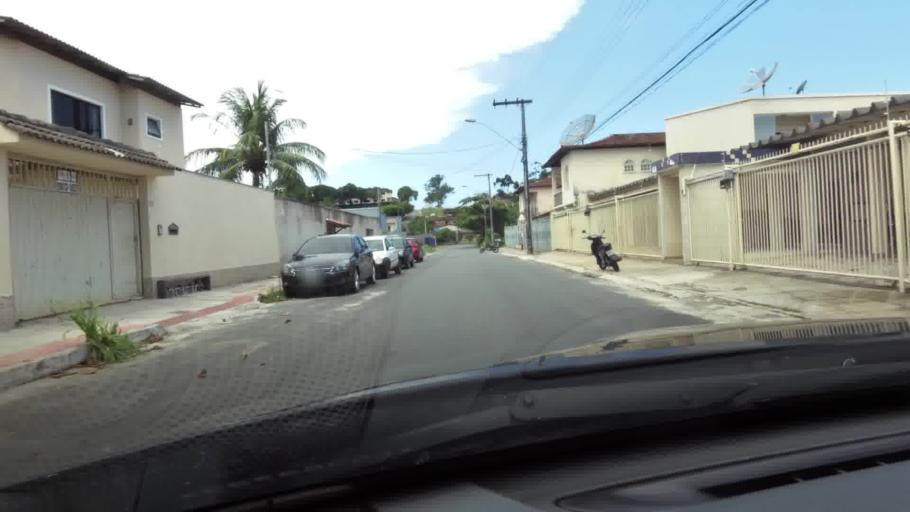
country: BR
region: Espirito Santo
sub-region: Guarapari
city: Guarapari
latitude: -20.6425
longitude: -40.4828
